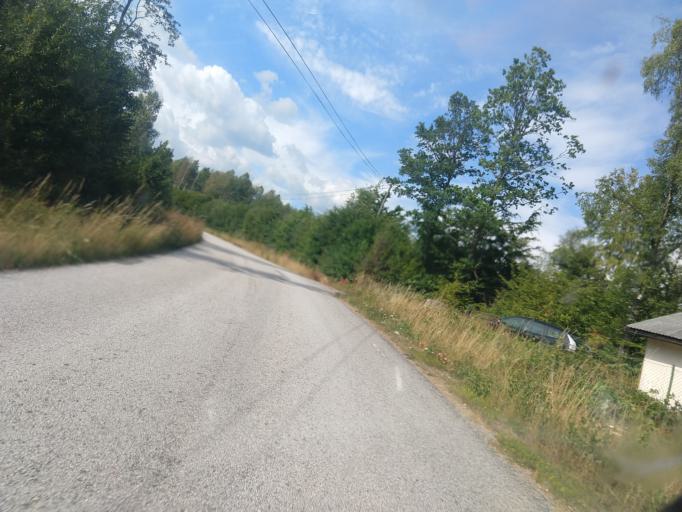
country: SE
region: Blekinge
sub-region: Karlskrona Kommun
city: Rodeby
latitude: 56.2322
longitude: 15.5801
